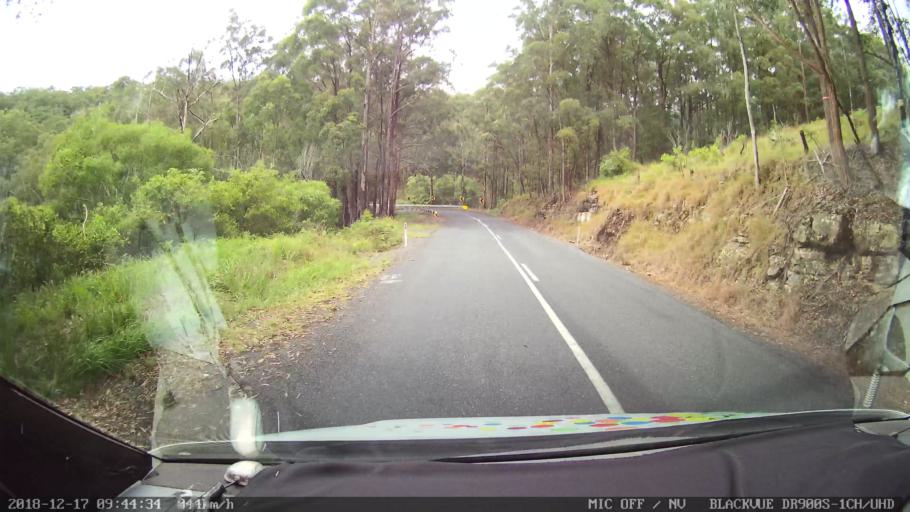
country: AU
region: New South Wales
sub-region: Tenterfield Municipality
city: Carrolls Creek
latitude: -28.9268
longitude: 152.3245
